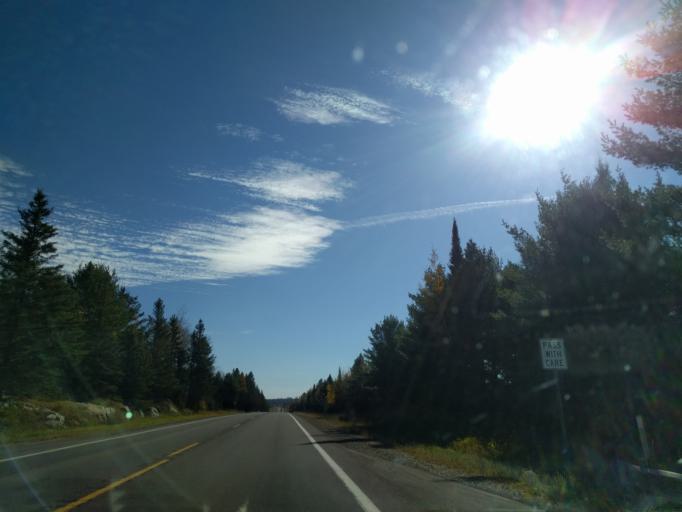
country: US
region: Michigan
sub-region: Marquette County
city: West Ishpeming
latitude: 46.3800
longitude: -87.9929
